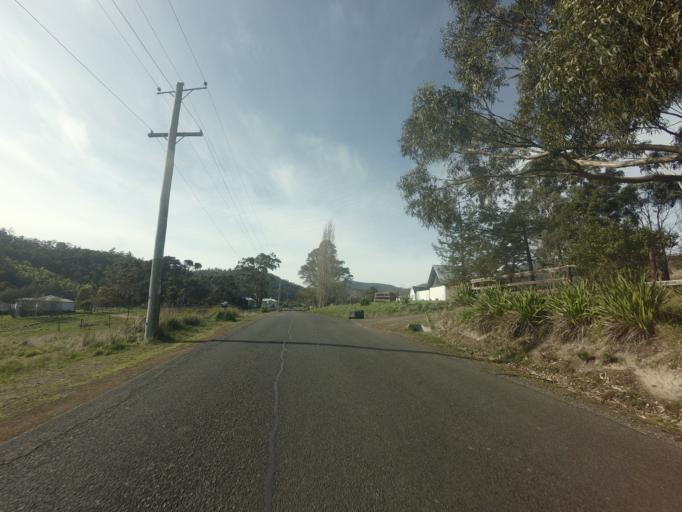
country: AU
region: Tasmania
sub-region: Huon Valley
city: Cygnet
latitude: -43.1812
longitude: 147.1255
